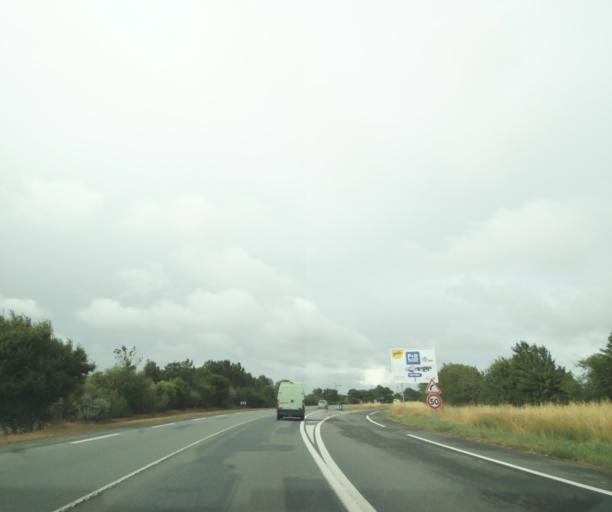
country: FR
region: Poitou-Charentes
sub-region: Departement de la Charente-Maritime
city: Lagord
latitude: 46.1932
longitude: -1.1415
